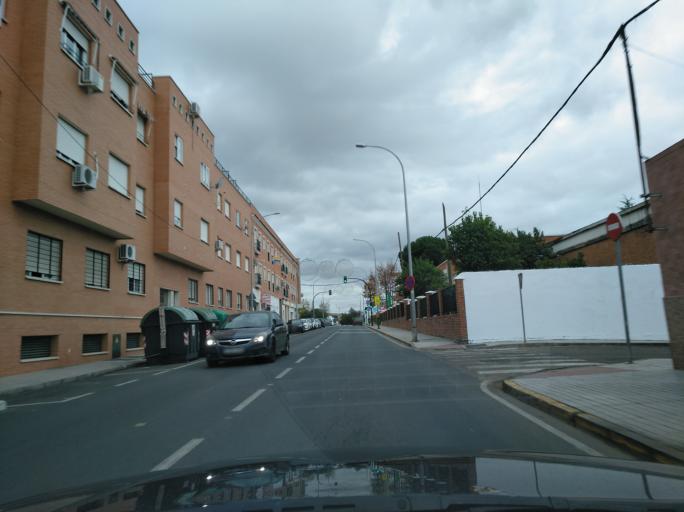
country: ES
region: Extremadura
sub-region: Provincia de Badajoz
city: Badajoz
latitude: 38.8913
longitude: -6.9784
